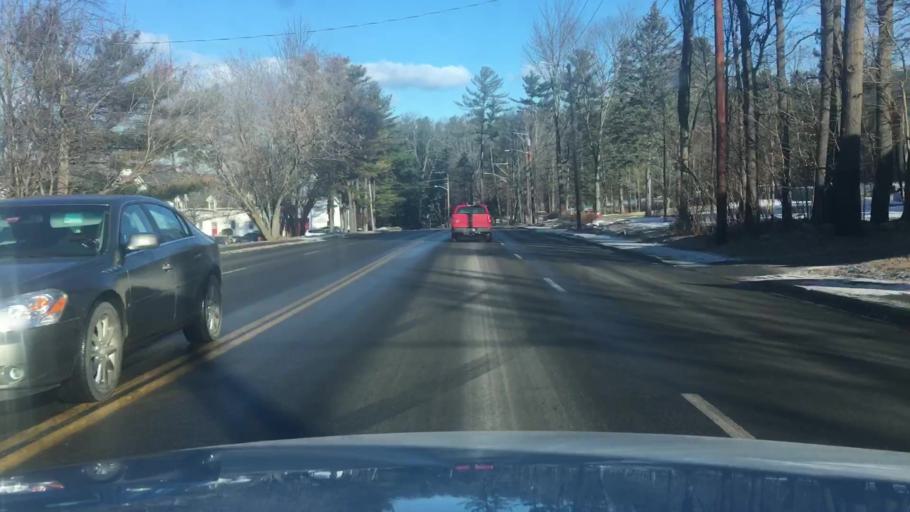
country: US
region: Maine
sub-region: Kennebec County
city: Augusta
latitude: 44.3114
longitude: -69.7645
